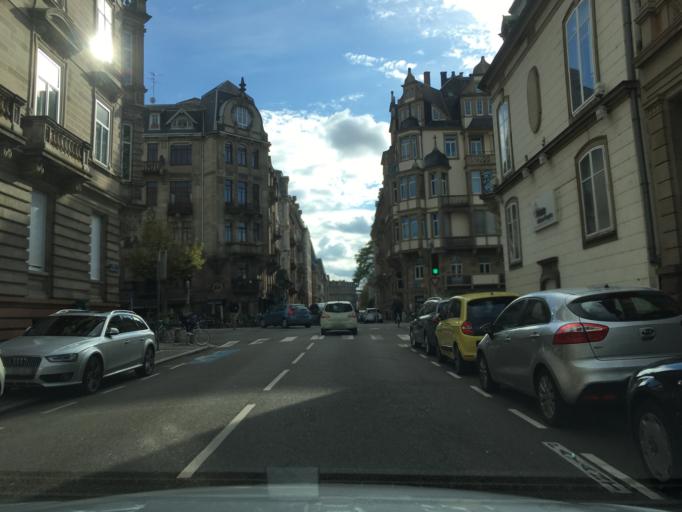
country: FR
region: Alsace
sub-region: Departement du Bas-Rhin
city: Strasbourg
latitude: 48.5883
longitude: 7.7574
